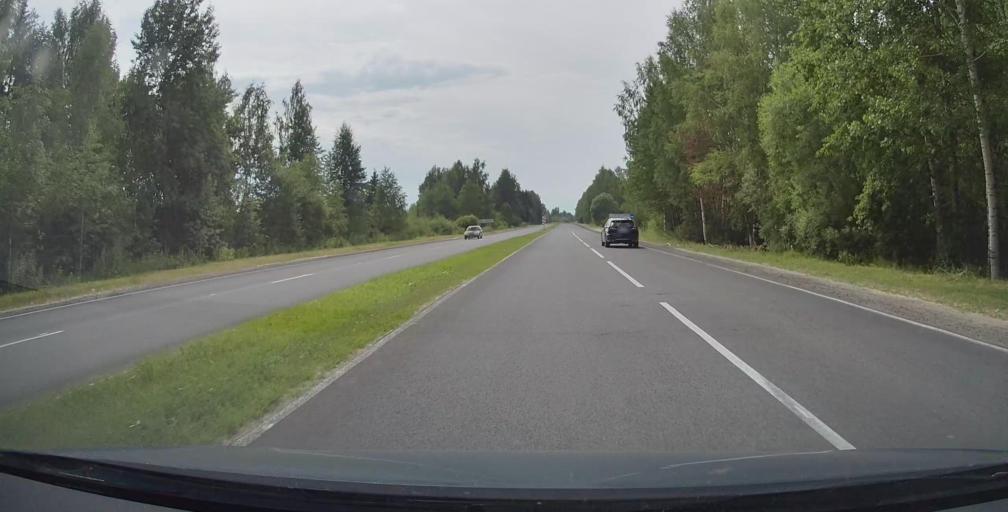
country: RU
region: Jaroslavl
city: Rybinsk
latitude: 58.0156
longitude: 38.9497
